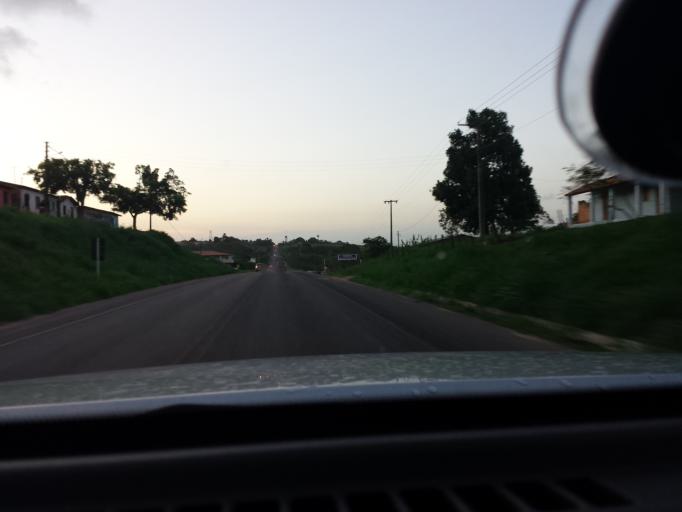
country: BR
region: Sergipe
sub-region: Salgado
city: Salgado
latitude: -10.9998
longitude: -37.5217
